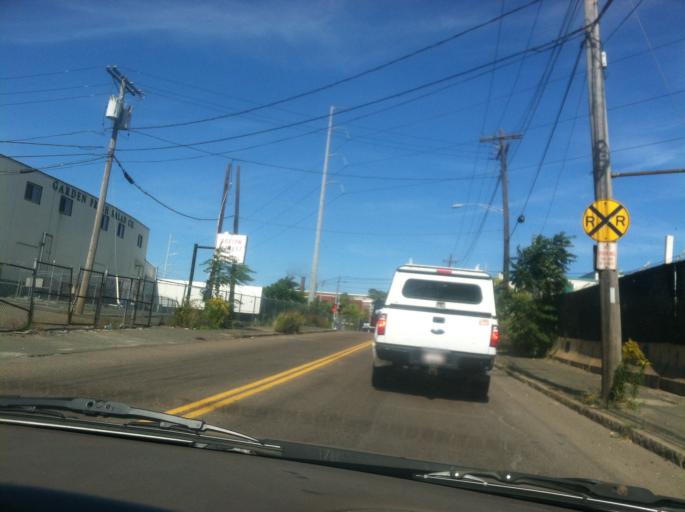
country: US
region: Massachusetts
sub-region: Suffolk County
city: Chelsea
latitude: 42.3864
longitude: -71.0227
